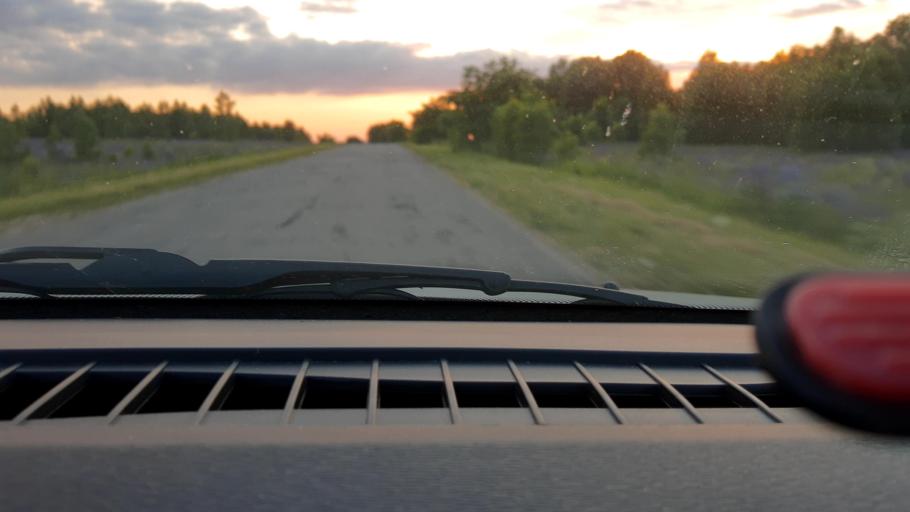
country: RU
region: Nizjnij Novgorod
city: Surovatikha
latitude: 55.8479
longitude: 43.9619
